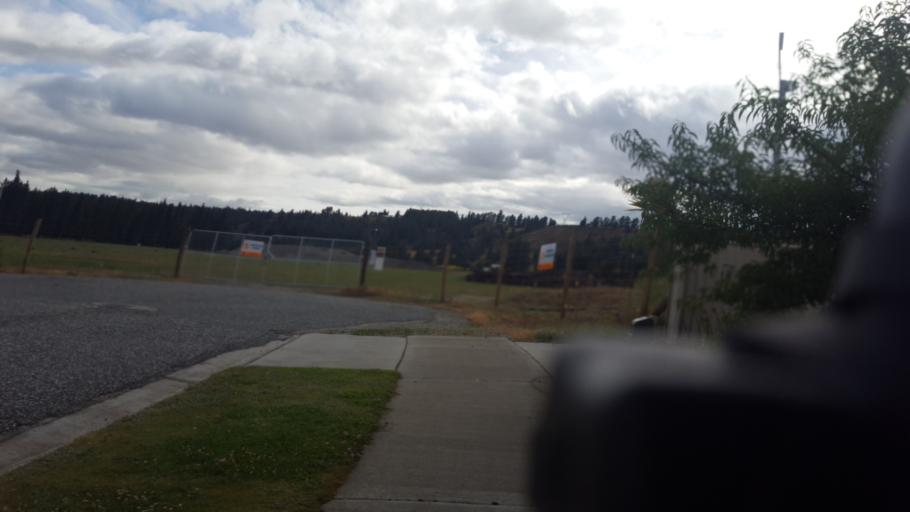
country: NZ
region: Otago
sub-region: Queenstown-Lakes District
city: Wanaka
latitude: -45.2389
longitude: 169.3819
